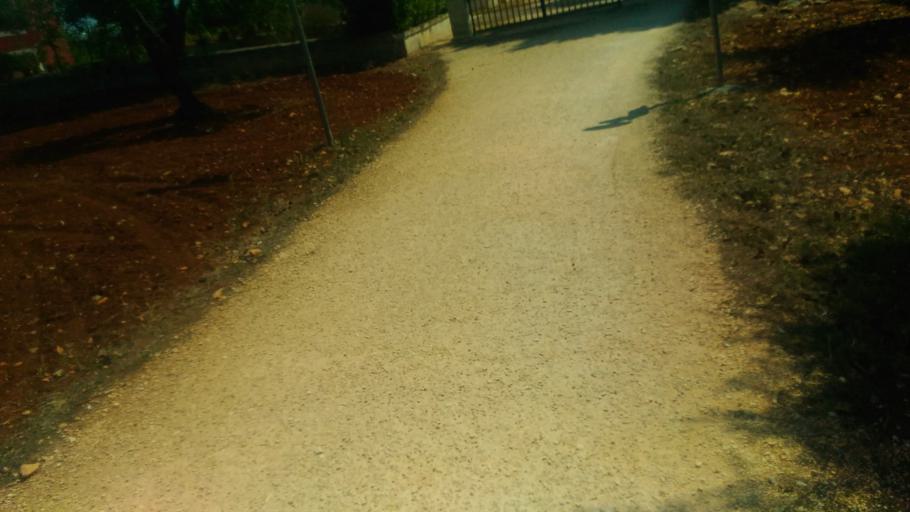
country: IT
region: Apulia
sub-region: Provincia di Brindisi
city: Cisternino
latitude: 40.7280
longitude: 17.3931
